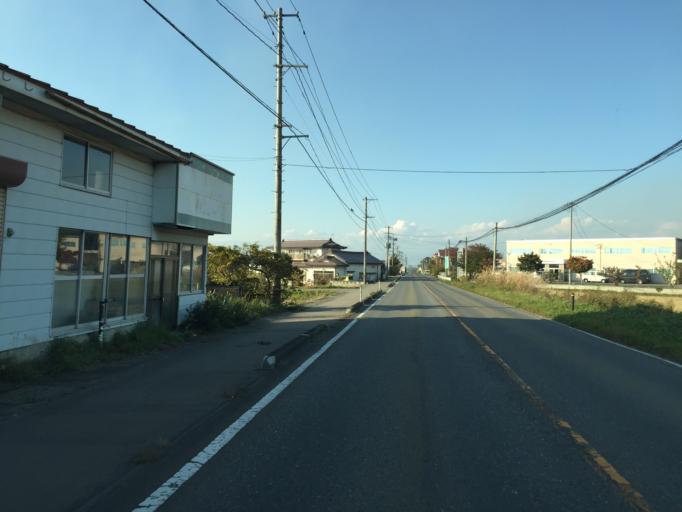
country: JP
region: Fukushima
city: Kitakata
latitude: 37.5396
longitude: 139.9139
